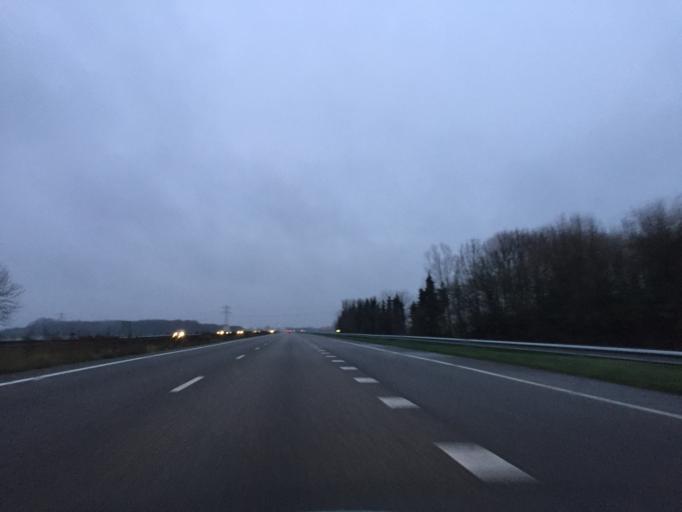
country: NL
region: North Brabant
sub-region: Gemeente Steenbergen
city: Kruisland
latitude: 51.5079
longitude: 4.3941
